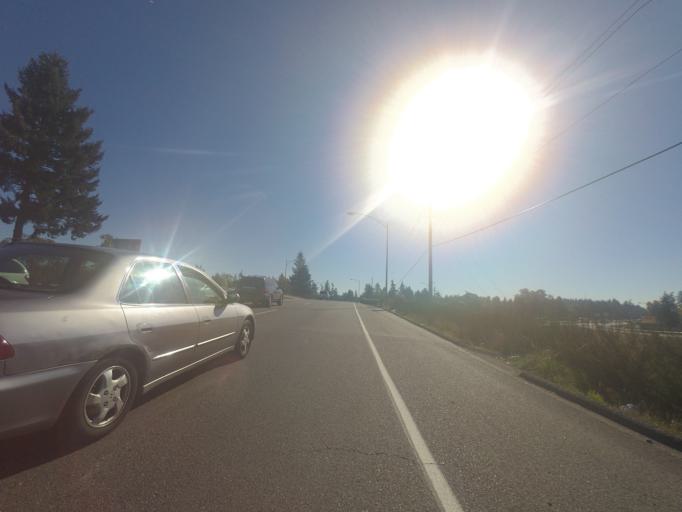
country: US
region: Washington
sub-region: Pierce County
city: McChord Air Force Base
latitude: 47.1480
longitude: -122.5046
